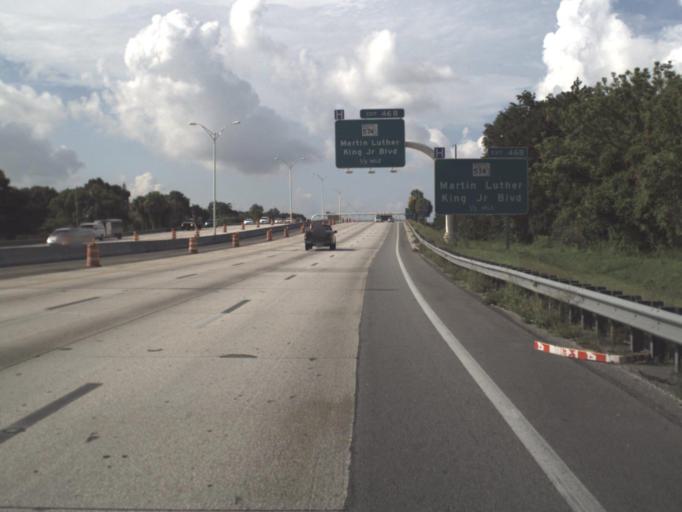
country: US
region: Florida
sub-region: Hillsborough County
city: Tampa
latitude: 27.9913
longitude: -82.4538
